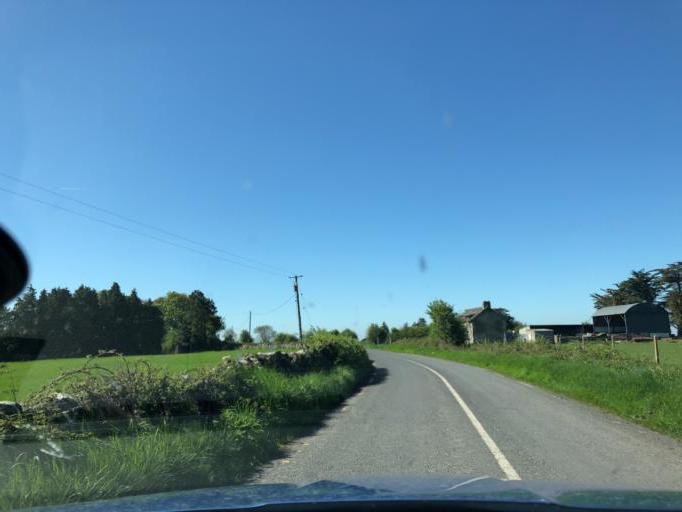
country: IE
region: Connaught
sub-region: County Galway
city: Portumna
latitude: 53.1703
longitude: -8.2104
